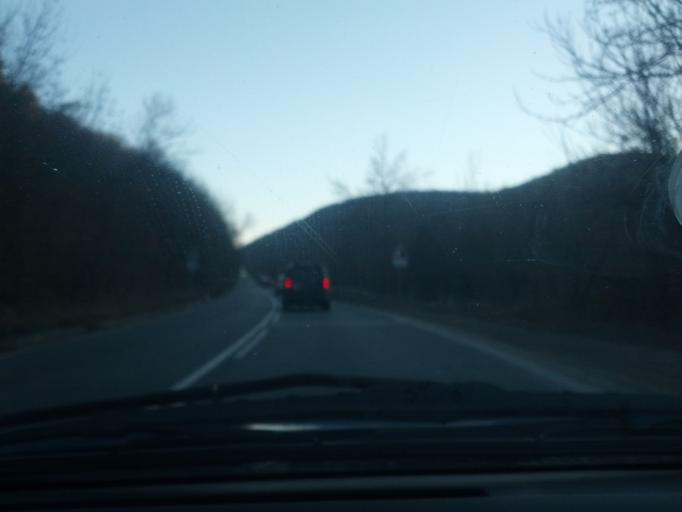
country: BG
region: Vratsa
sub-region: Obshtina Mezdra
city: Mezdra
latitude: 43.1078
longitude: 23.6793
